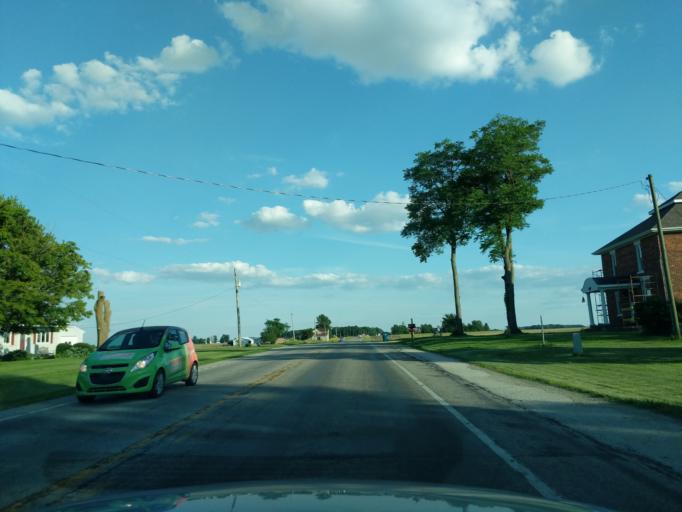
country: US
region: Indiana
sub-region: Huntington County
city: Huntington
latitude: 40.8132
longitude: -85.4649
